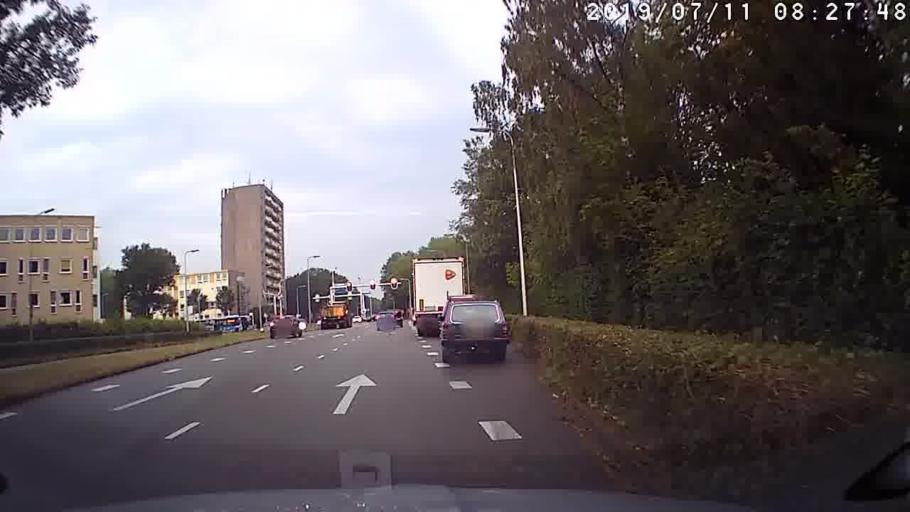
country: NL
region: Overijssel
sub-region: Gemeente Zwolle
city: Zwolle
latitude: 52.5042
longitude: 6.1151
